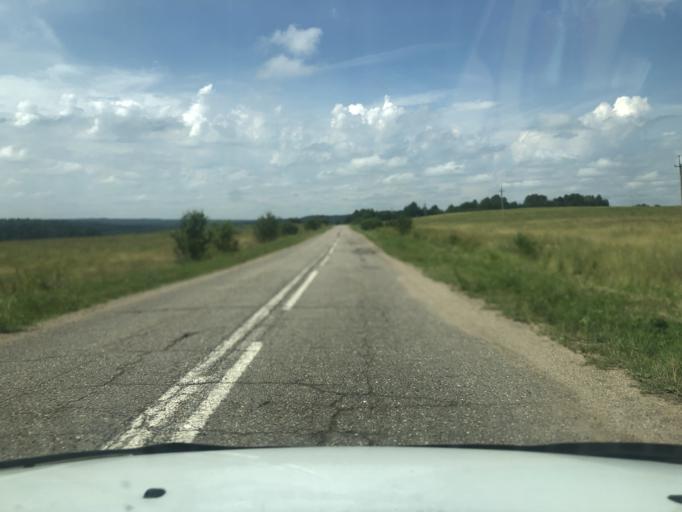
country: RU
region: Jaroslavl
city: Pereslavl'-Zalesskiy
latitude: 57.0390
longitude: 38.8854
